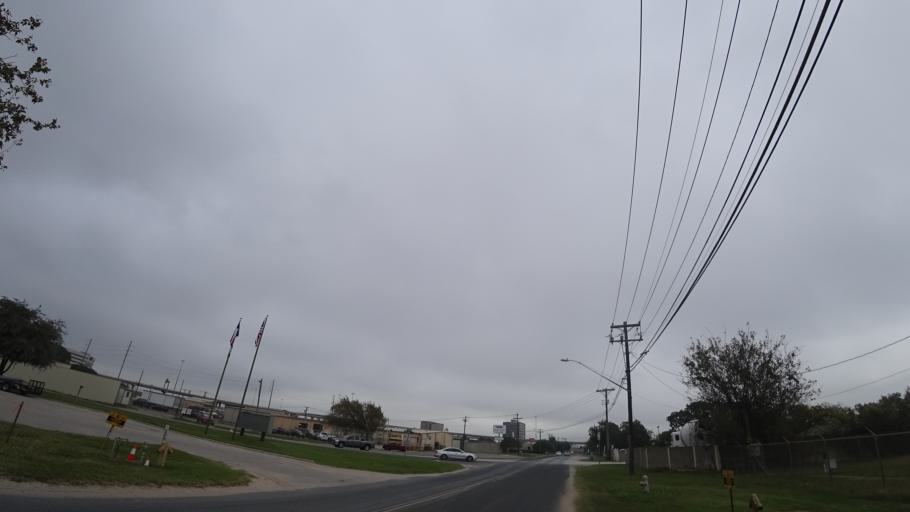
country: US
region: Texas
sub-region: Travis County
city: Austin
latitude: 30.2151
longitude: -97.7578
